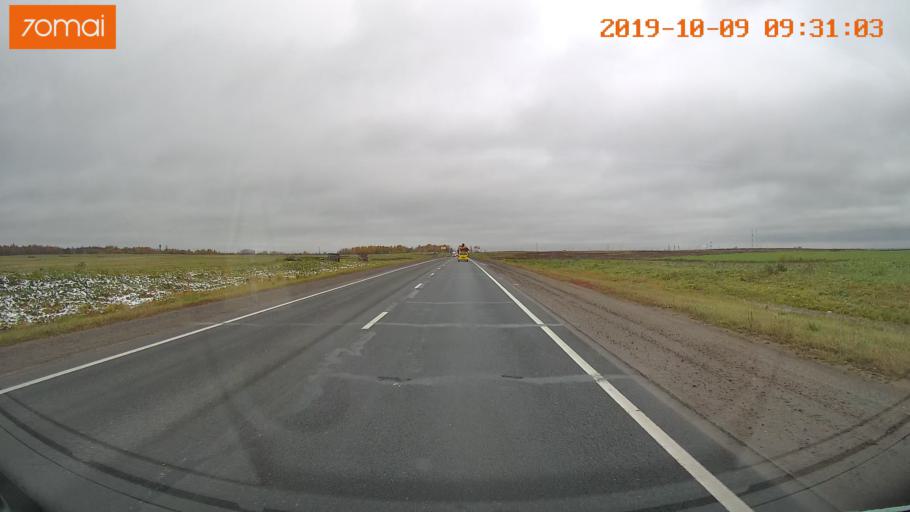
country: RU
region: Vologda
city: Vologda
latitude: 59.1460
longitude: 39.9425
